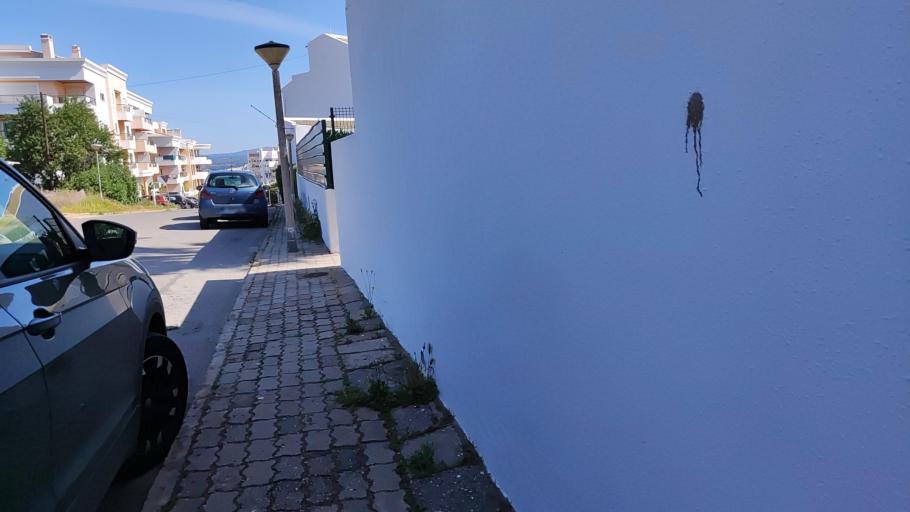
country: PT
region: Faro
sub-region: Lagos
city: Lagos
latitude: 37.0935
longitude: -8.6823
